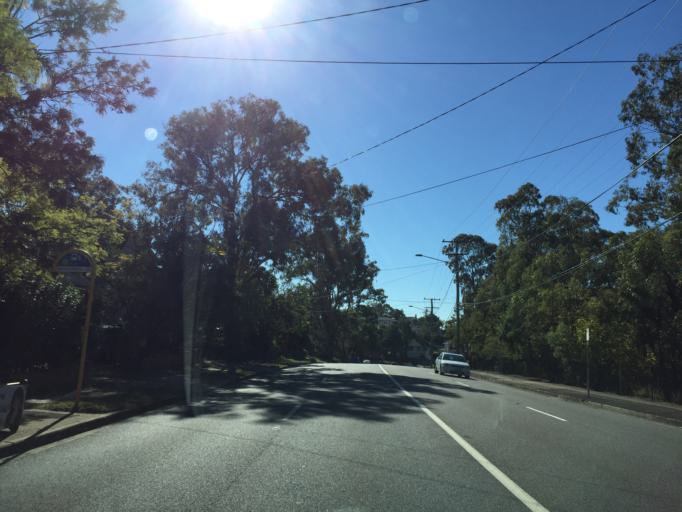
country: AU
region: Queensland
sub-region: Brisbane
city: Everton Park
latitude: -27.4109
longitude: 152.9652
